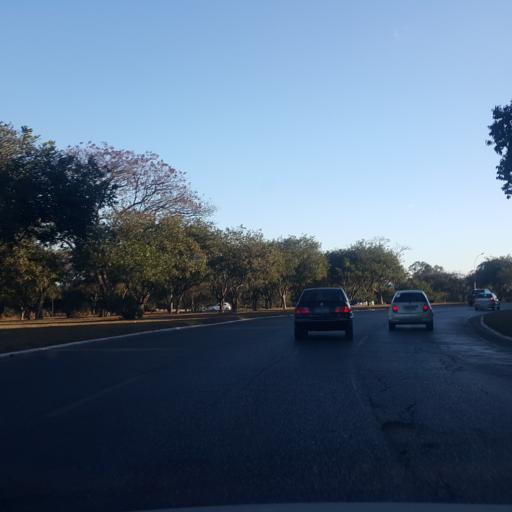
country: BR
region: Federal District
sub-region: Brasilia
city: Brasilia
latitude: -15.8427
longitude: -47.9315
